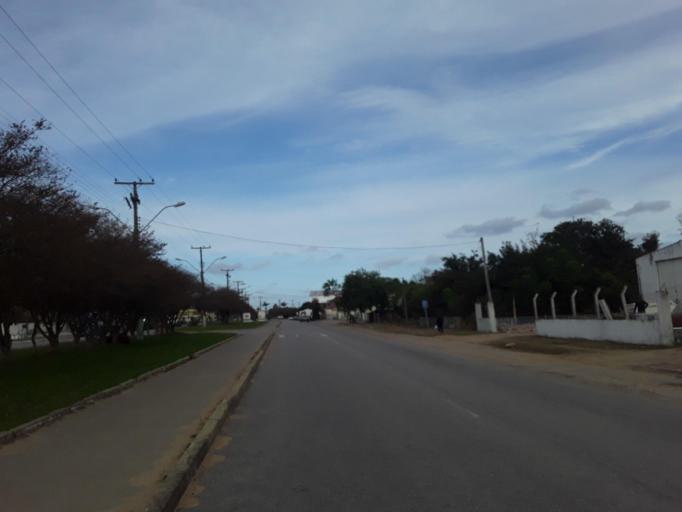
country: BR
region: Rio Grande do Sul
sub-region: Sao Lourenco Do Sul
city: Sao Lourenco do Sul
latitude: -31.3508
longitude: -51.9908
